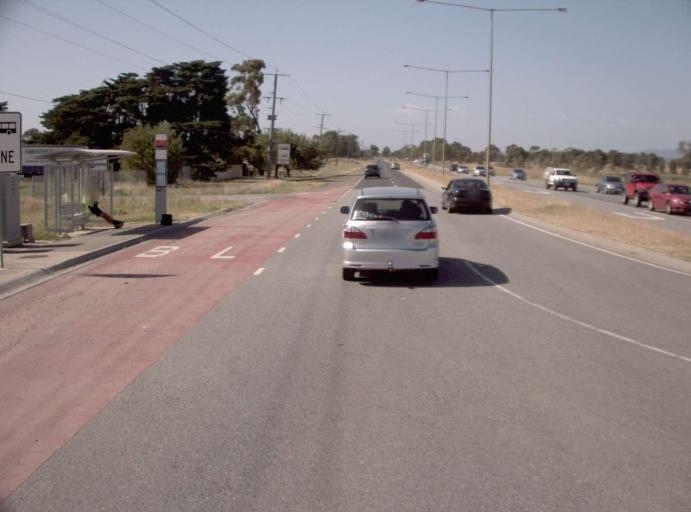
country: AU
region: Victoria
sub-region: Frankston
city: Sandhurst
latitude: -38.0483
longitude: 145.2086
